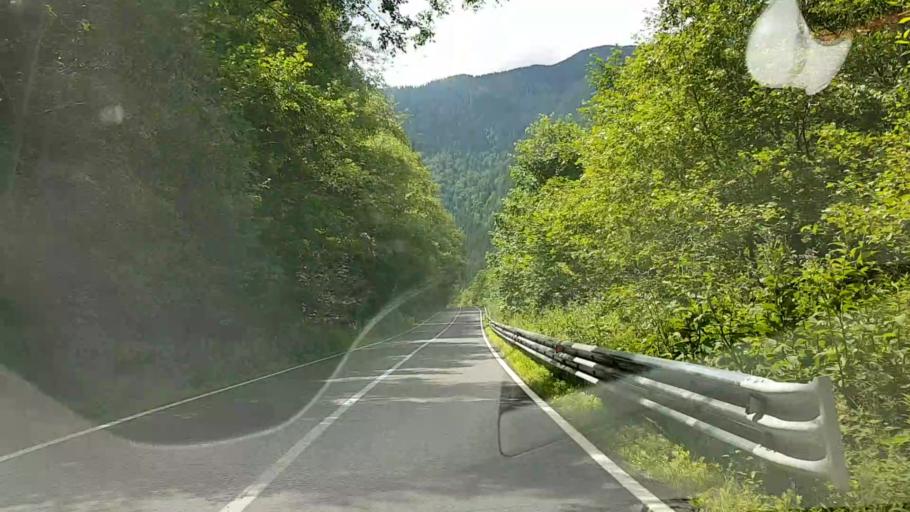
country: RO
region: Suceava
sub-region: Comuna Crucea
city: Crucea
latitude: 47.3867
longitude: 25.5810
